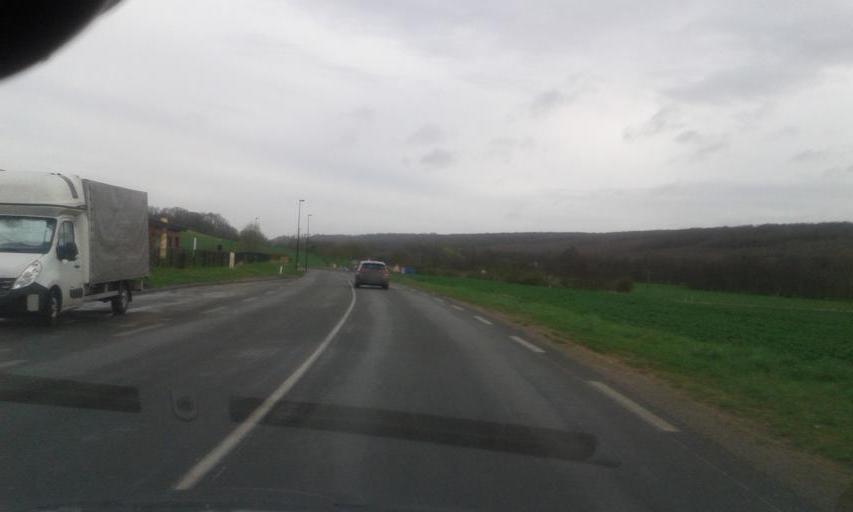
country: FR
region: Haute-Normandie
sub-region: Departement de l'Eure
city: Charleval
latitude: 49.3766
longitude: 1.3748
